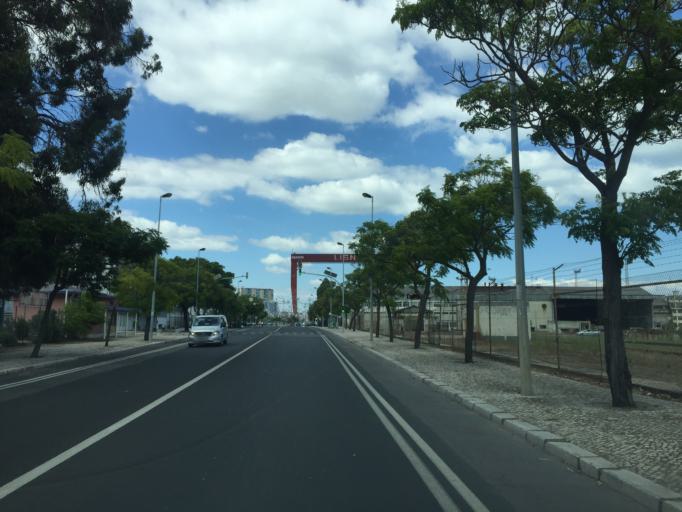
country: PT
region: Setubal
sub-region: Almada
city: Almada
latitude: 38.6760
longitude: -9.1520
